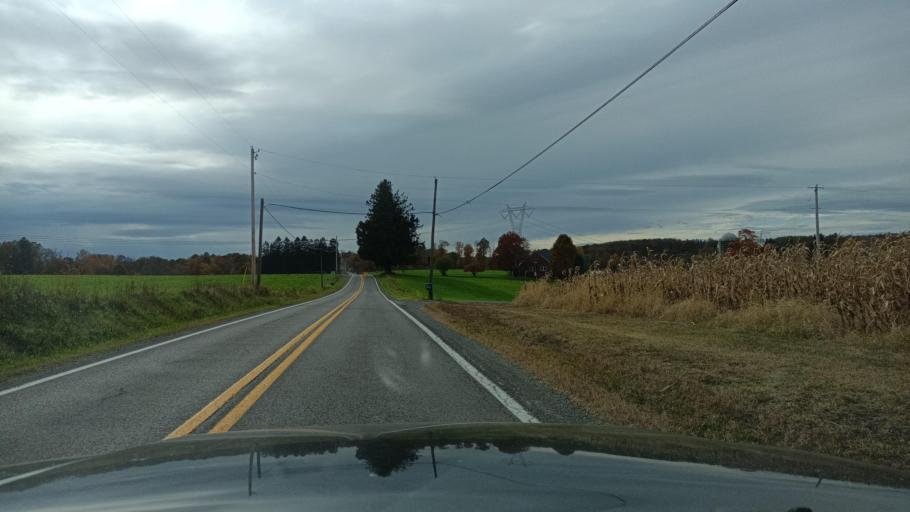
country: US
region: West Virginia
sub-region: Preston County
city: Terra Alta
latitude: 39.3162
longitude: -79.5758
